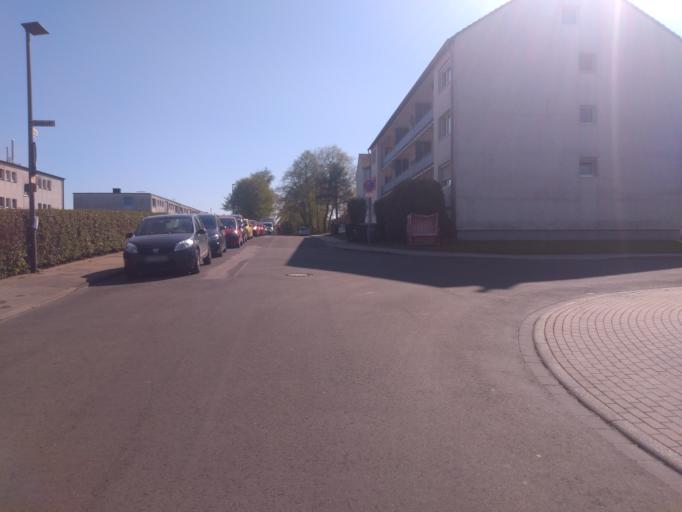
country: DE
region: North Rhine-Westphalia
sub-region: Regierungsbezirk Dusseldorf
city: Velbert
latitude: 51.3060
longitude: 7.1045
